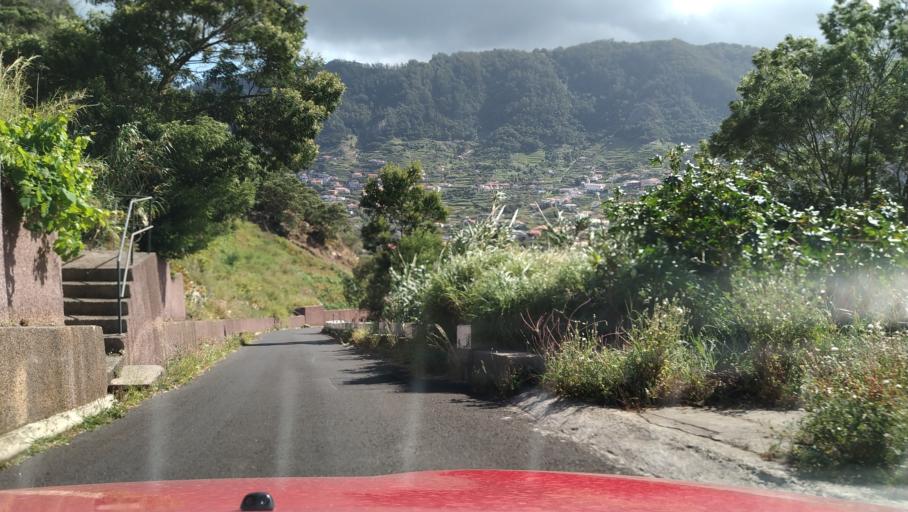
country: PT
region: Madeira
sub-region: Machico
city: Canical
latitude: 32.7367
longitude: -16.7744
